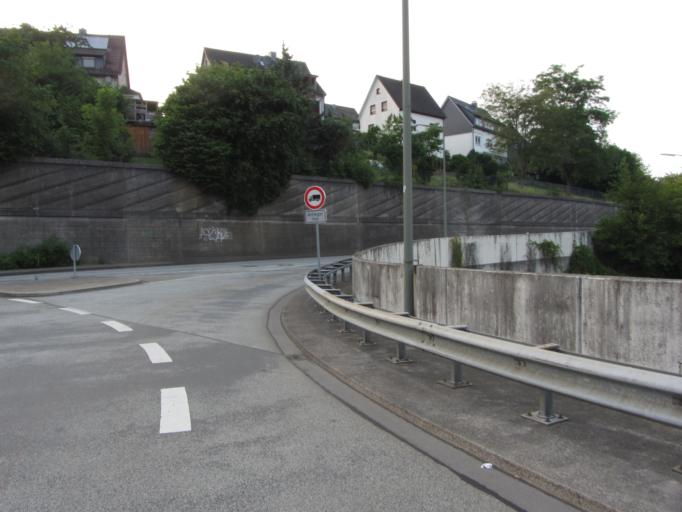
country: DE
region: North Rhine-Westphalia
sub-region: Regierungsbezirk Arnsberg
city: Siegen
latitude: 50.8527
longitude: 7.9931
